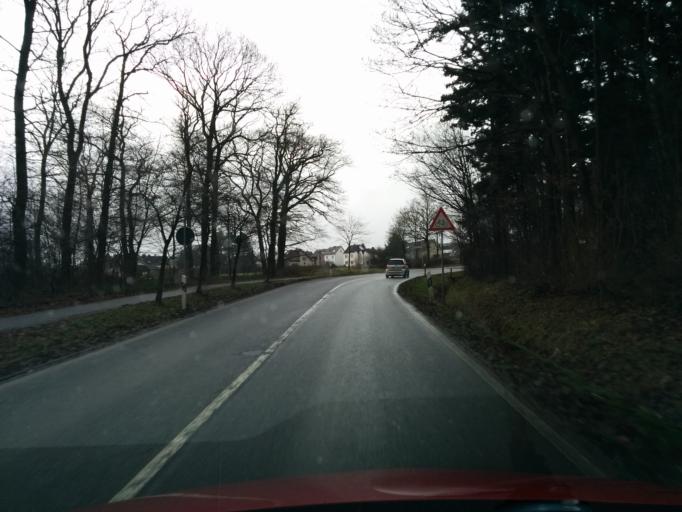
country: DE
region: North Rhine-Westphalia
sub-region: Regierungsbezirk Koln
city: Rheinbach
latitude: 50.6054
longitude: 6.9360
